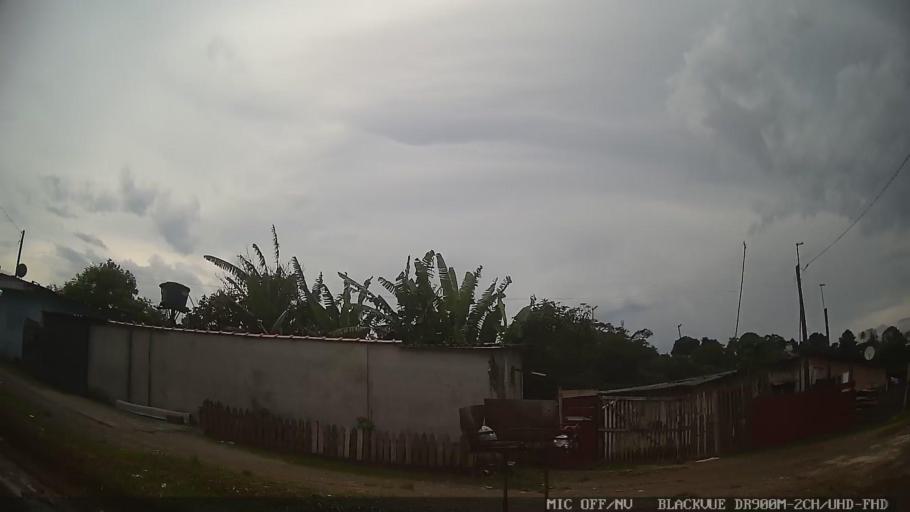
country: BR
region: Sao Paulo
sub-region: Itaquaquecetuba
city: Itaquaquecetuba
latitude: -23.4702
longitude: -46.2989
